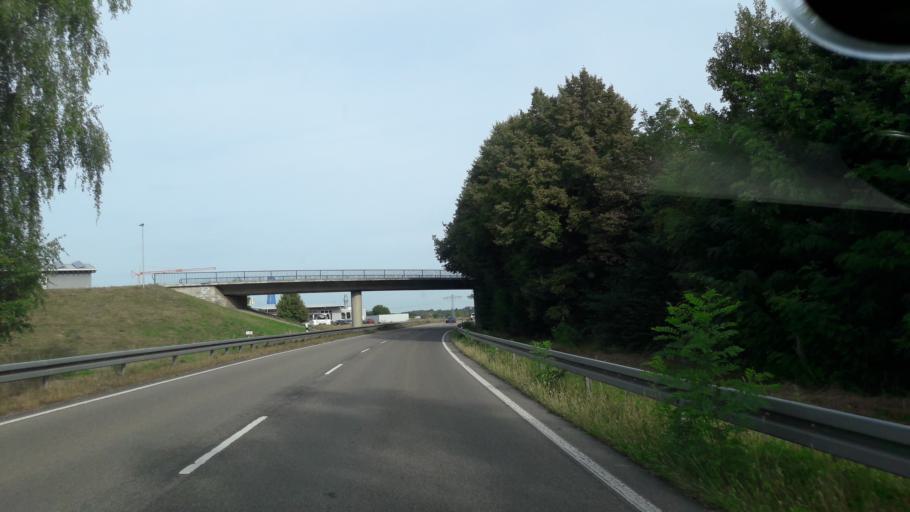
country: DE
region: Baden-Wuerttemberg
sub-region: Karlsruhe Region
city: Kronau
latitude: 49.2130
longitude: 8.6304
